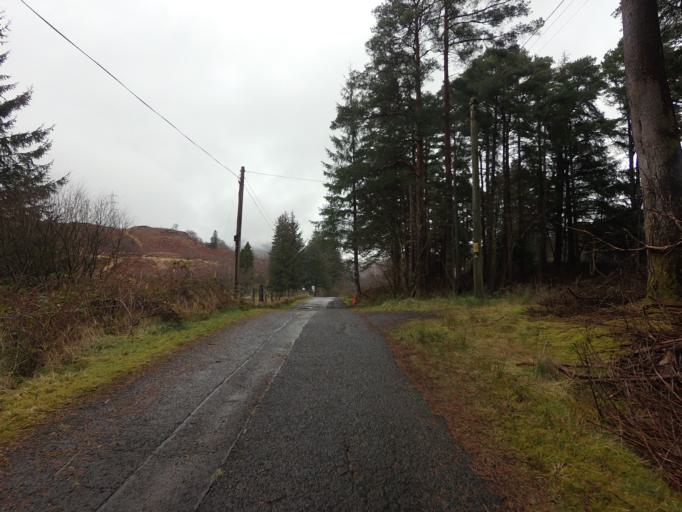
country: GB
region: Scotland
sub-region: West Dunbartonshire
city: Balloch
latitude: 56.2575
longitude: -4.5825
